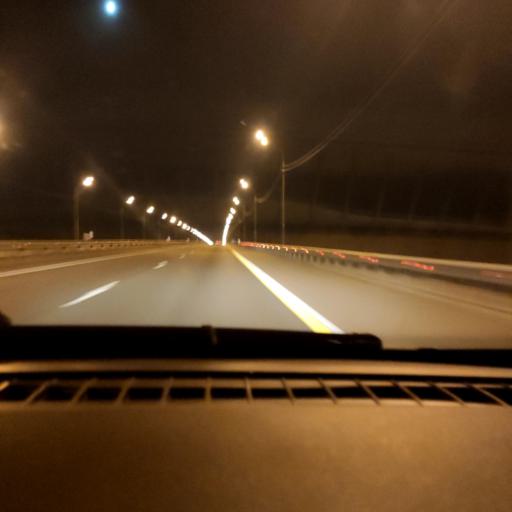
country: RU
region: Lipetsk
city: Khlevnoye
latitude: 52.1974
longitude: 39.1699
